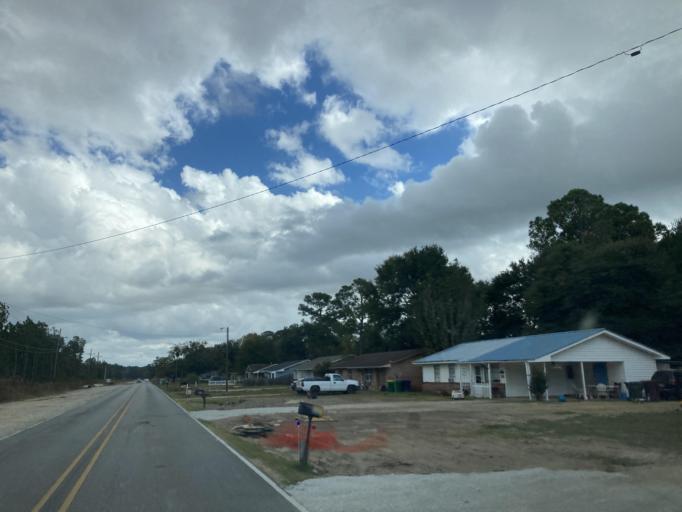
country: US
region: Mississippi
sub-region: Jackson County
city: Gulf Hills
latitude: 30.4390
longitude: -88.8230
